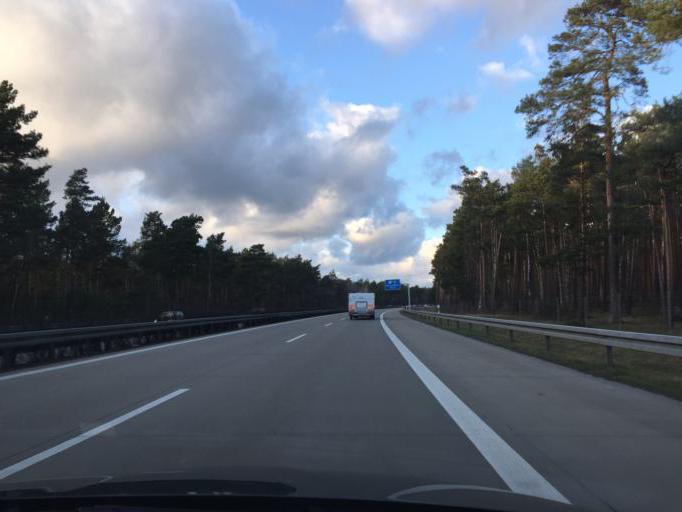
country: DE
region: Brandenburg
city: Halbe
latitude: 52.0515
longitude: 13.6573
